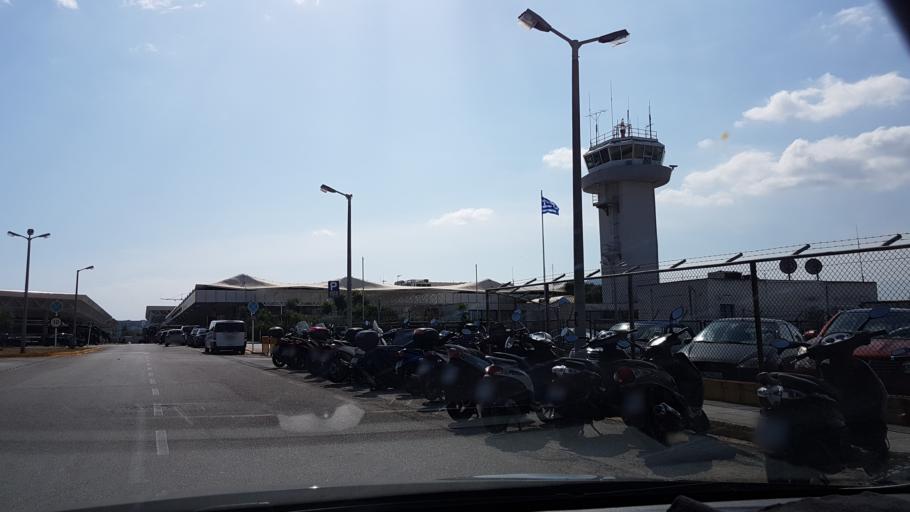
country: GR
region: Ionian Islands
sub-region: Nomos Kerkyras
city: Kerkyra
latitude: 39.6088
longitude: 19.9145
